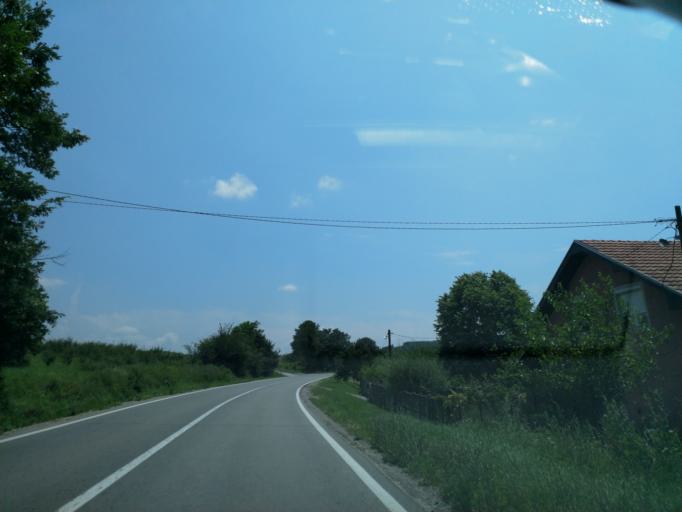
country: RS
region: Central Serbia
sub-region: Toplicki Okrug
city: Blace
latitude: 43.3129
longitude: 21.2463
